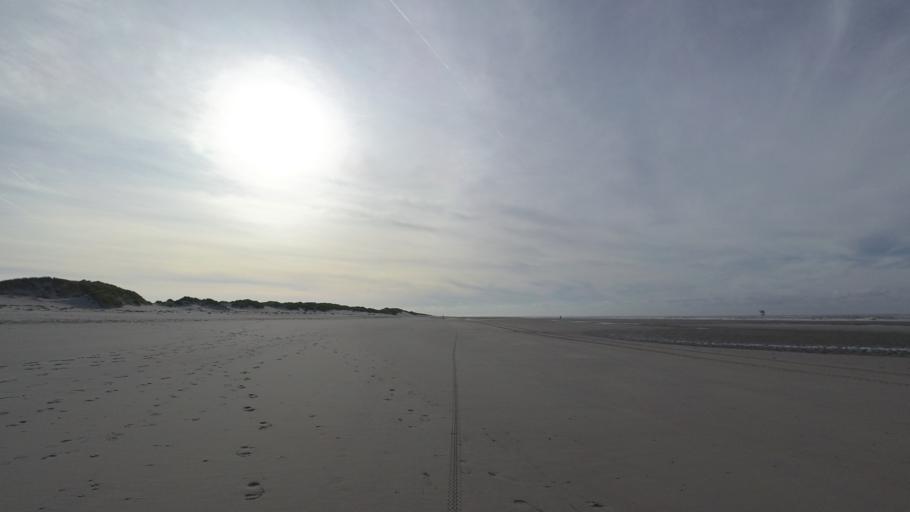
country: NL
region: Friesland
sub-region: Gemeente Dongeradeel
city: Holwerd
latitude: 53.4675
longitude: 5.9062
